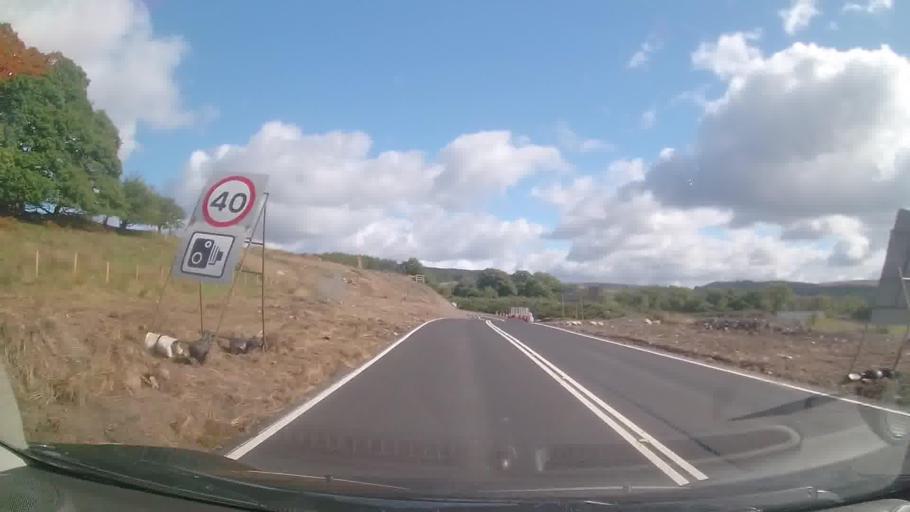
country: GB
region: Wales
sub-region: Rhondda Cynon Taf
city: Hirwaun
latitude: 51.7507
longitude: -3.4706
